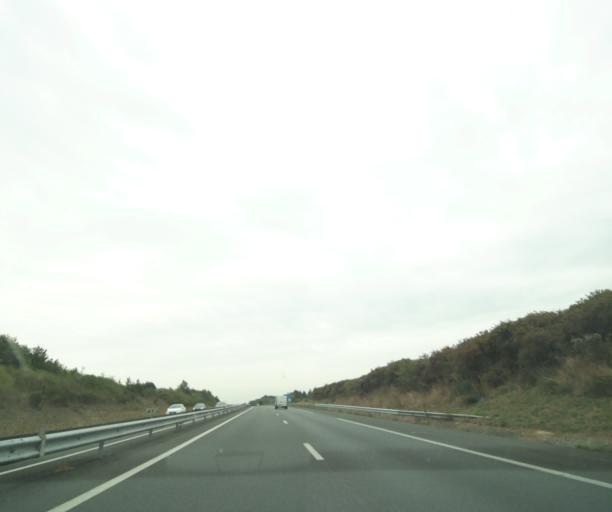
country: FR
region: Pays de la Loire
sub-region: Departement de la Vendee
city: Les Essarts
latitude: 46.7793
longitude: -1.1909
